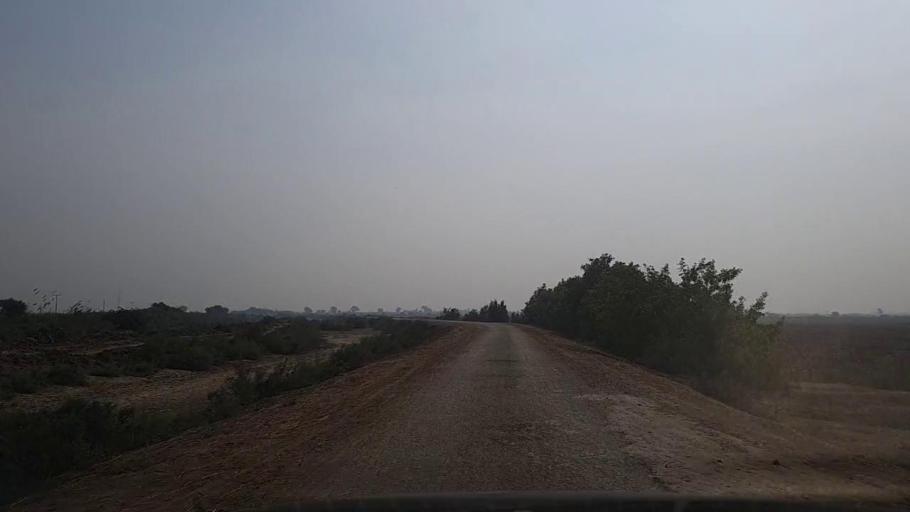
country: PK
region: Sindh
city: Mirpur Sakro
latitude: 24.3836
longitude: 67.7533
